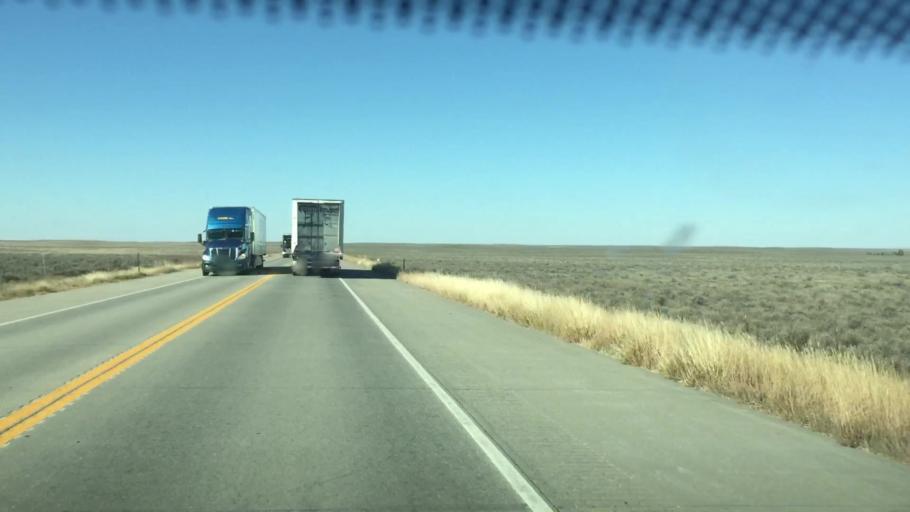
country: US
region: Colorado
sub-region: Kiowa County
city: Eads
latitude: 38.5468
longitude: -102.7859
